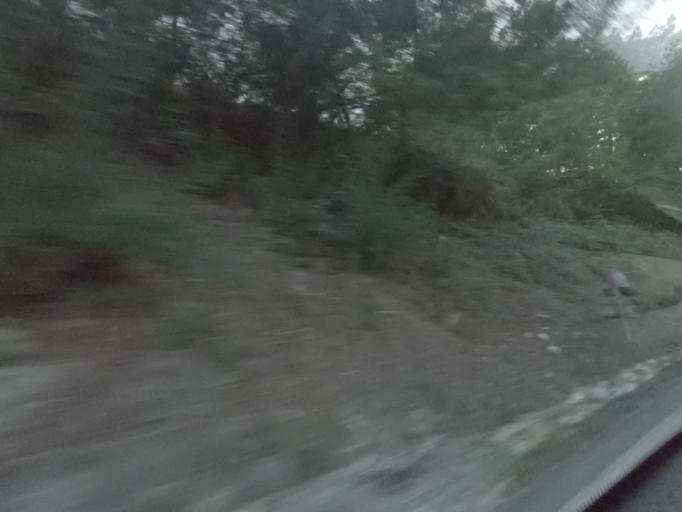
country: PT
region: Viseu
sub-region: Armamar
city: Armamar
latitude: 41.1280
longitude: -7.7355
